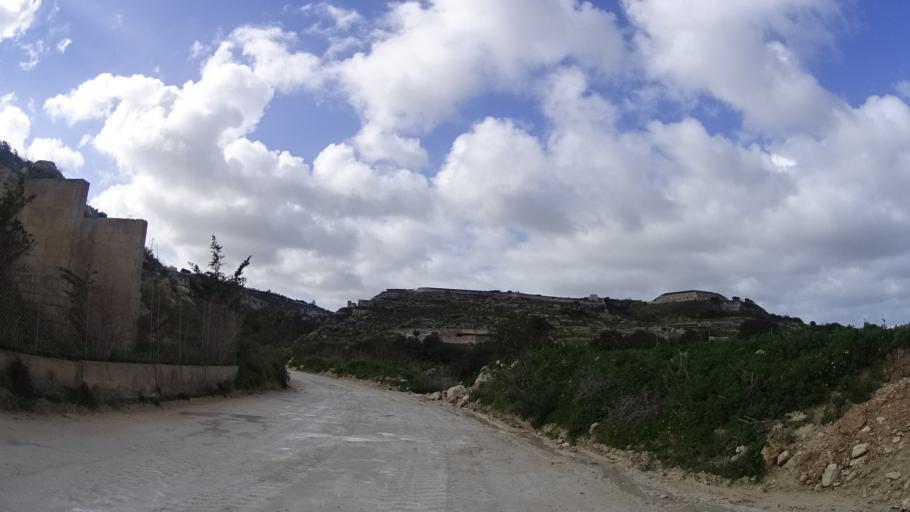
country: MT
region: In-Naxxar
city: Naxxar
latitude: 35.9242
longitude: 14.4328
